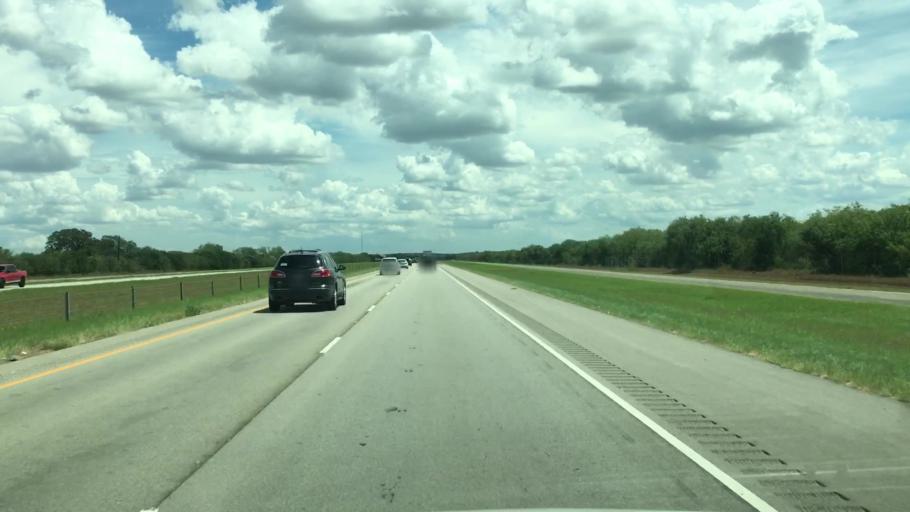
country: US
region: Texas
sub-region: Live Oak County
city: George West
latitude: 28.2798
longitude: -97.9550
